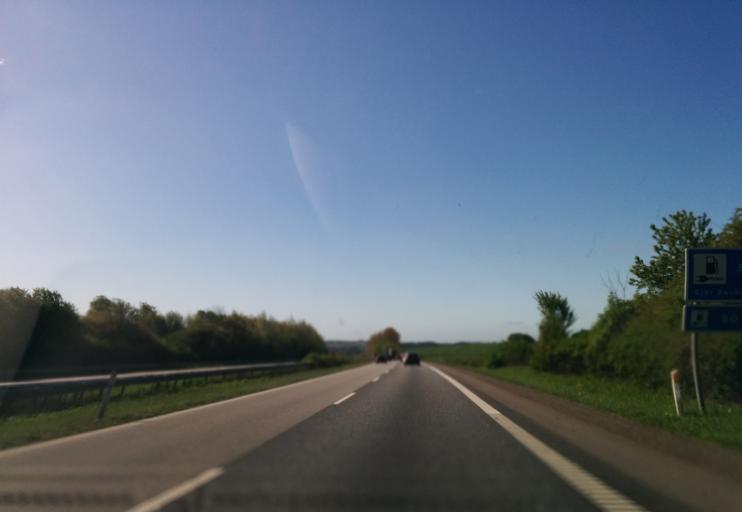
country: DK
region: Central Jutland
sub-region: Skanderborg Kommune
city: Skanderborg
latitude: 56.0281
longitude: 9.8815
